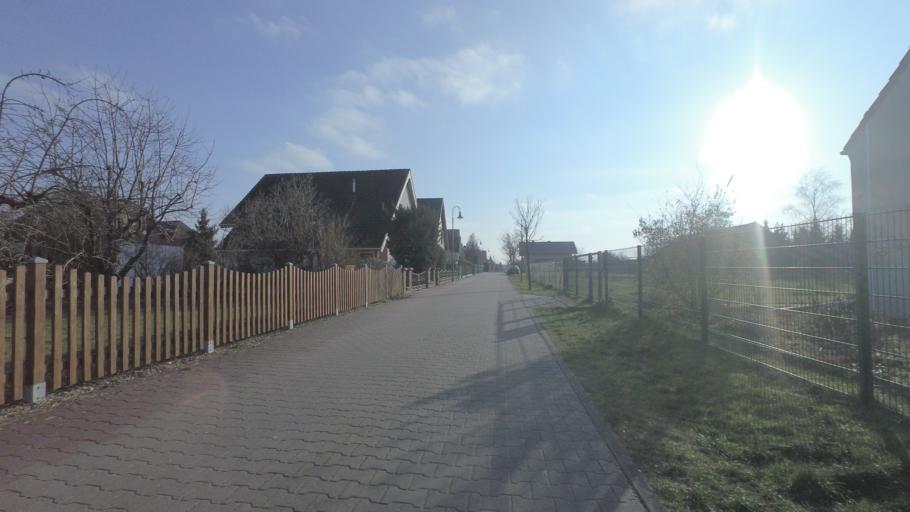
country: DE
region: Brandenburg
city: Rangsdorf
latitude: 52.2515
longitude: 13.3816
